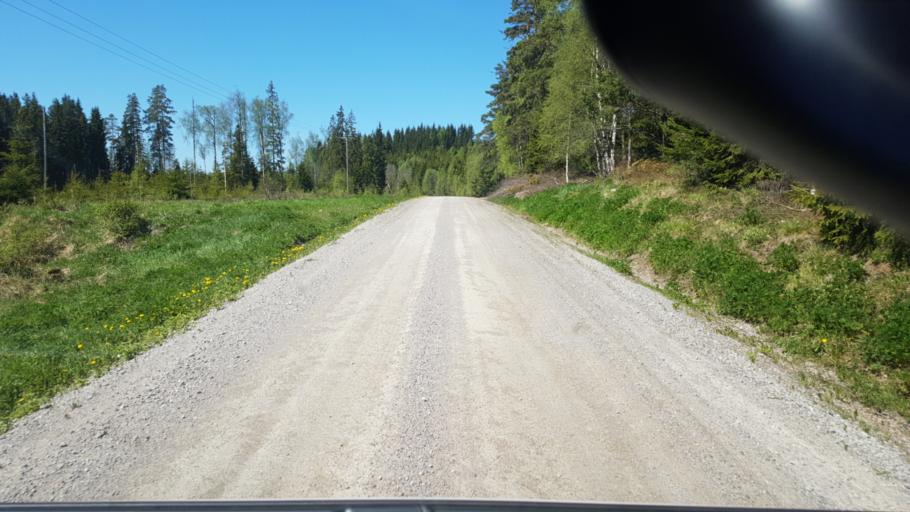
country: SE
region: Vaermland
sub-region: Arvika Kommun
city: Arvika
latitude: 59.8400
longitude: 12.7398
